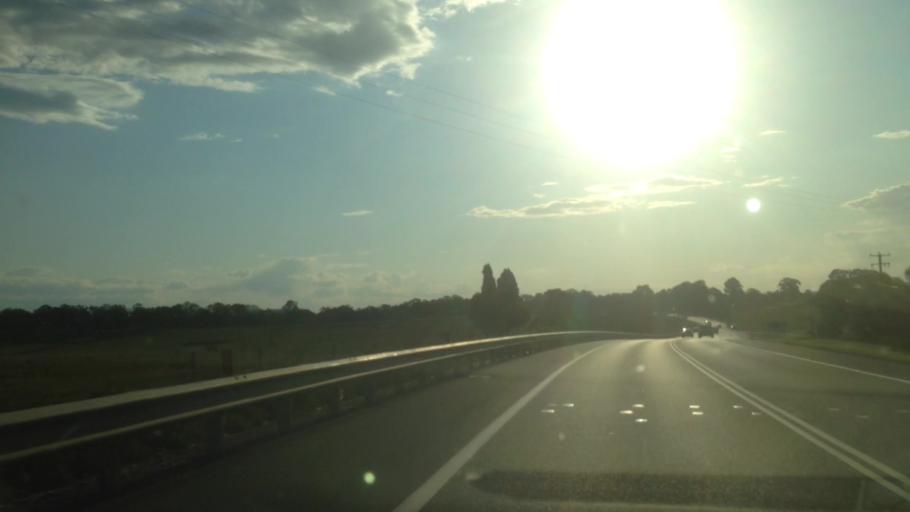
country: AU
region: New South Wales
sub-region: Cessnock
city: Heddon Greta
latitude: -32.8302
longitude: 151.5219
